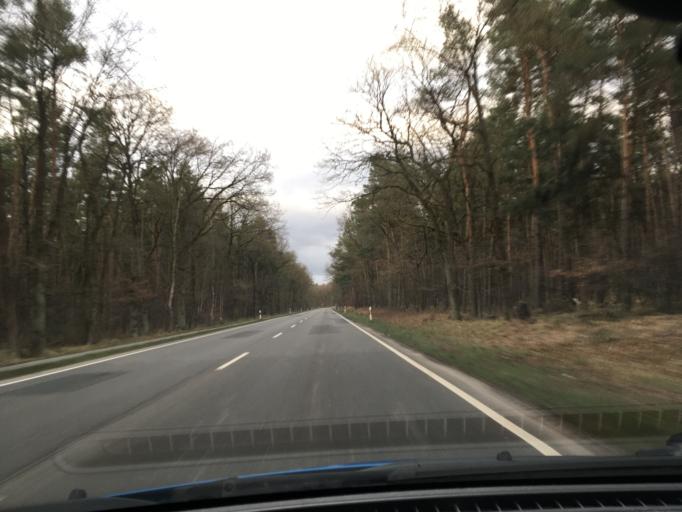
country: DE
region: Lower Saxony
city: Adendorf
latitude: 53.3079
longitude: 10.4300
